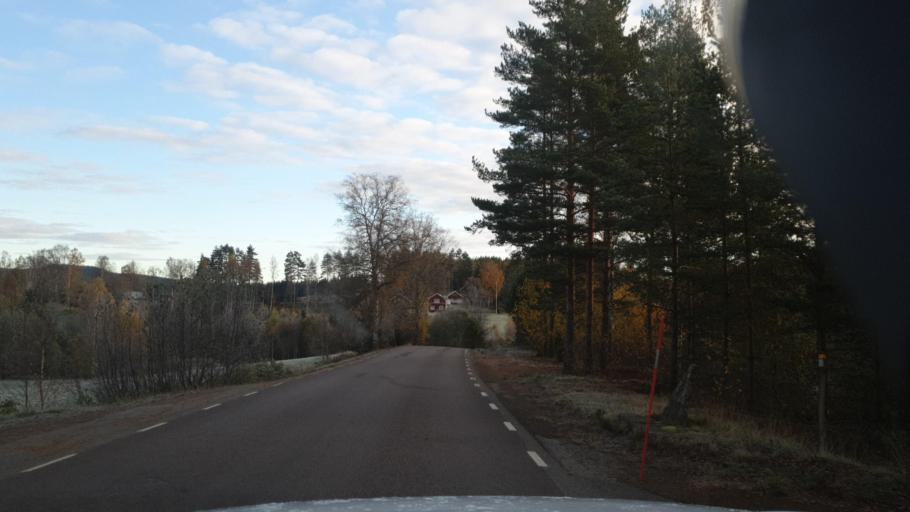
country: SE
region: Vaermland
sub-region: Eda Kommun
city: Charlottenberg
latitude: 59.7878
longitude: 12.2196
